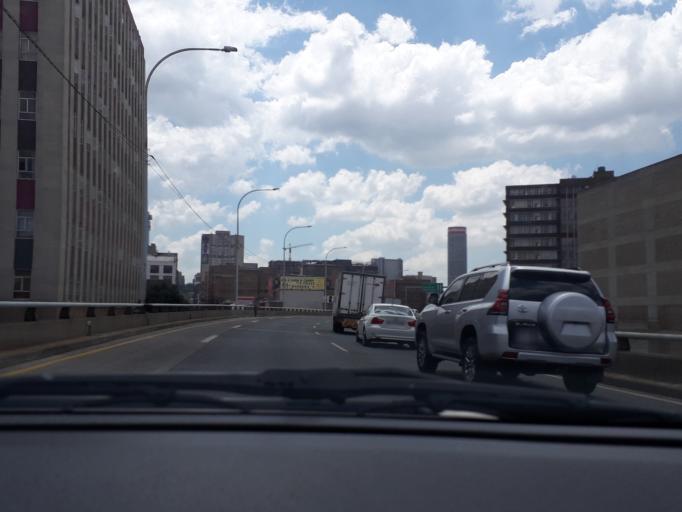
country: ZA
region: Gauteng
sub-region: City of Johannesburg Metropolitan Municipality
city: Johannesburg
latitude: -26.2051
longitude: 28.0544
